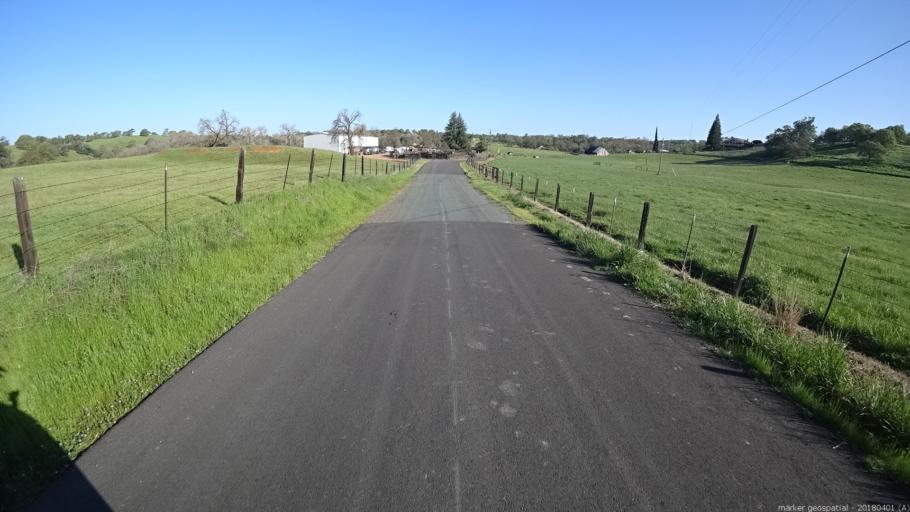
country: US
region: California
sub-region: Sacramento County
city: Rancho Murieta
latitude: 38.4968
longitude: -121.0464
